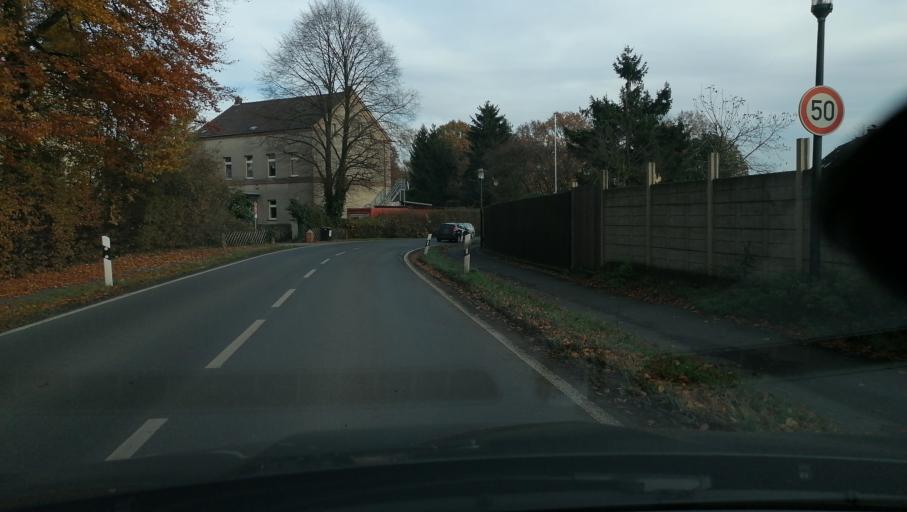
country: DE
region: North Rhine-Westphalia
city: Castrop-Rauxel
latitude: 51.5788
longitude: 7.2659
